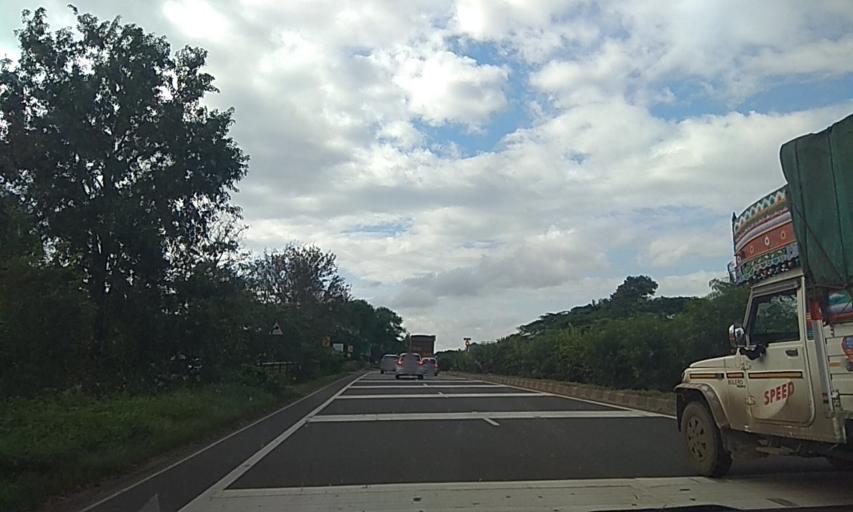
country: IN
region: Maharashtra
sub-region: Satara Division
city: Karad
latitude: 17.1232
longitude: 74.1926
